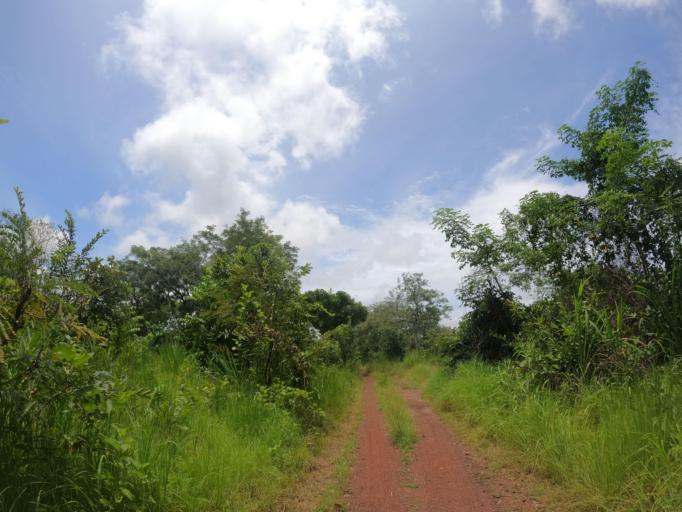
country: SL
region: Northern Province
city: Makeni
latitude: 9.1485
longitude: -12.2511
